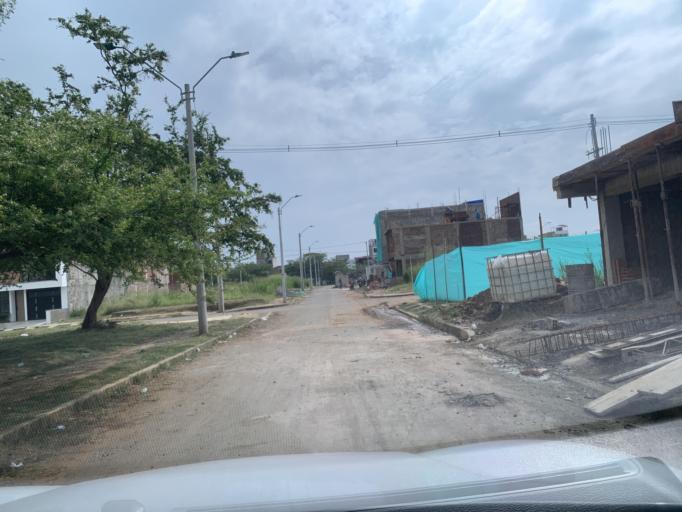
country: CO
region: Valle del Cauca
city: Cali
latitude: 3.3929
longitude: -76.5211
